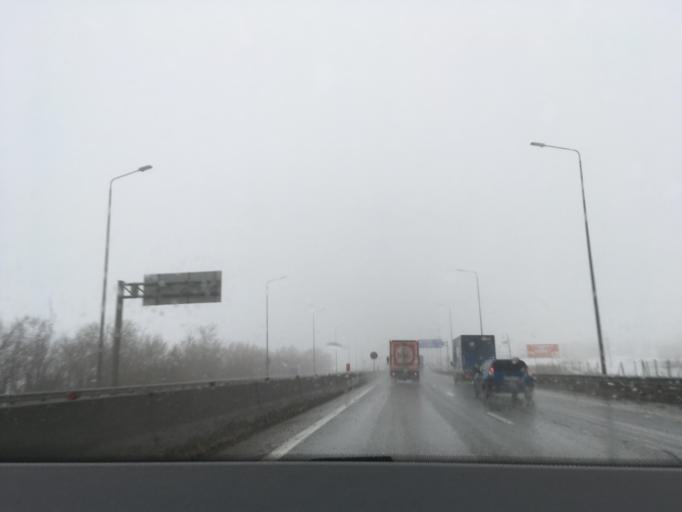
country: RU
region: Rostov
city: Samarskoye
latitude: 47.0070
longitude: 39.7321
